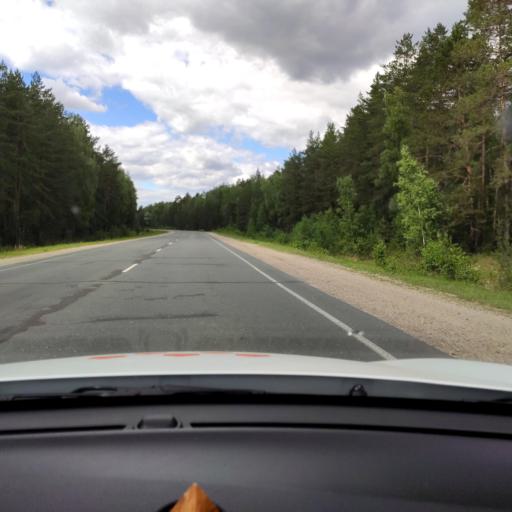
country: RU
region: Mariy-El
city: Krasnogorskiy
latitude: 56.1204
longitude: 48.3437
